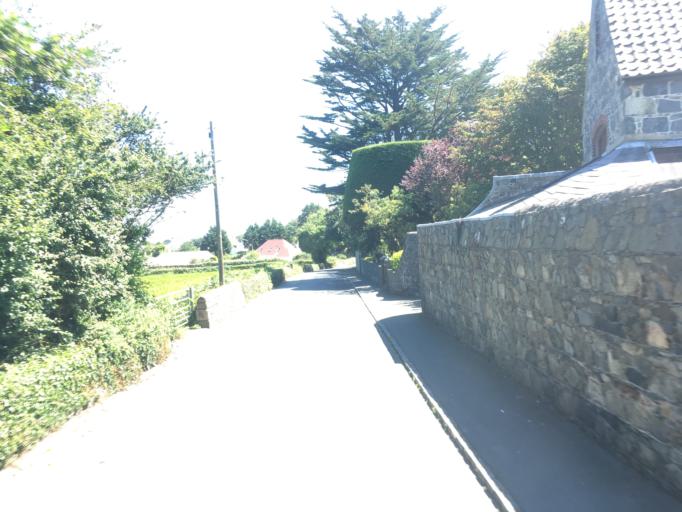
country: GG
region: St Peter Port
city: Saint Peter Port
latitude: 49.4887
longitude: -2.5142
